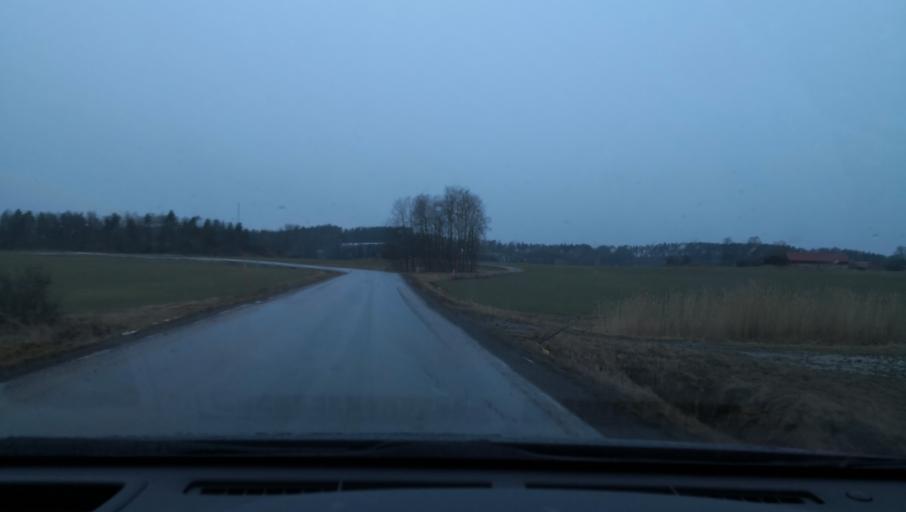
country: SE
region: Soedermanland
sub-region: Eskilstuna Kommun
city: Arla
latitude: 59.4054
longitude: 16.6833
